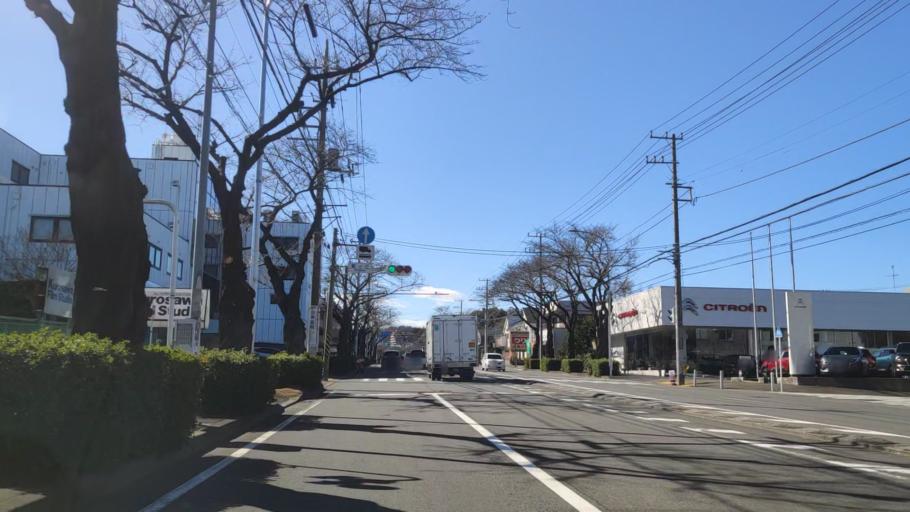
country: JP
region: Tokyo
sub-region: Machida-shi
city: Machida
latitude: 35.5191
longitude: 139.5051
